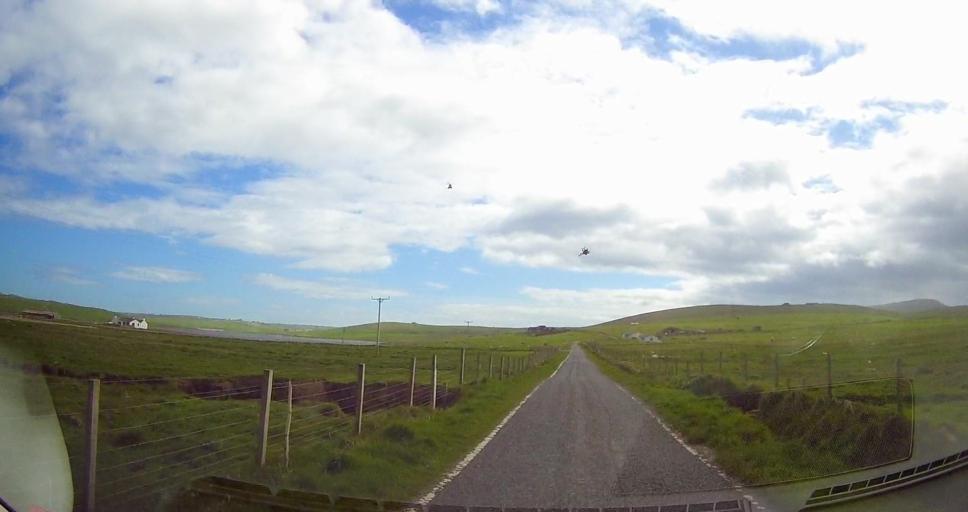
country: GB
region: Scotland
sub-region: Shetland Islands
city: Sandwick
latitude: 59.9374
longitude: -1.3461
